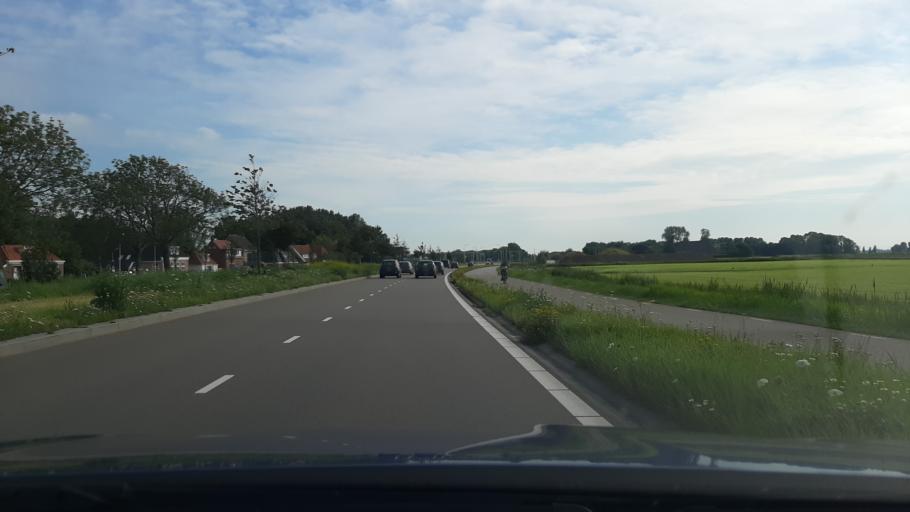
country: NL
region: Friesland
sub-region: Gemeente Leeuwarden
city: Goutum
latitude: 53.1763
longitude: 5.7946
